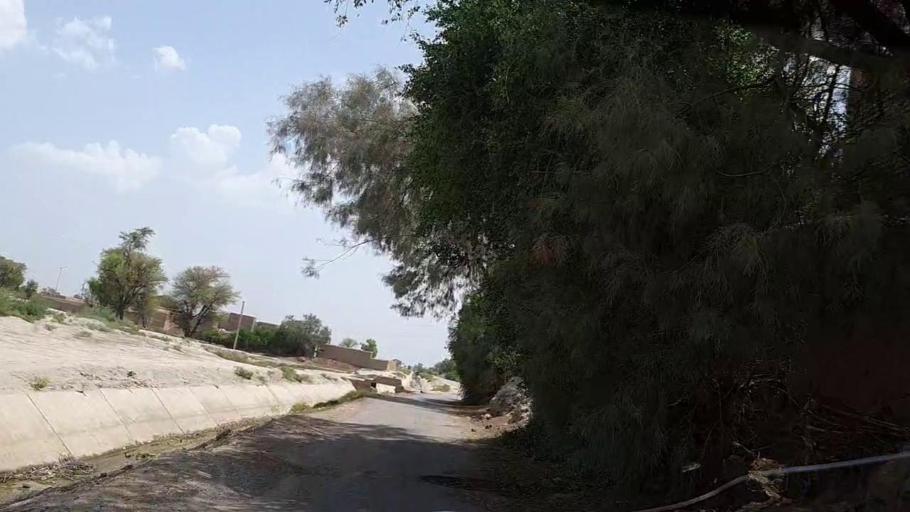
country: PK
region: Sindh
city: Bhan
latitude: 26.5386
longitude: 67.6335
